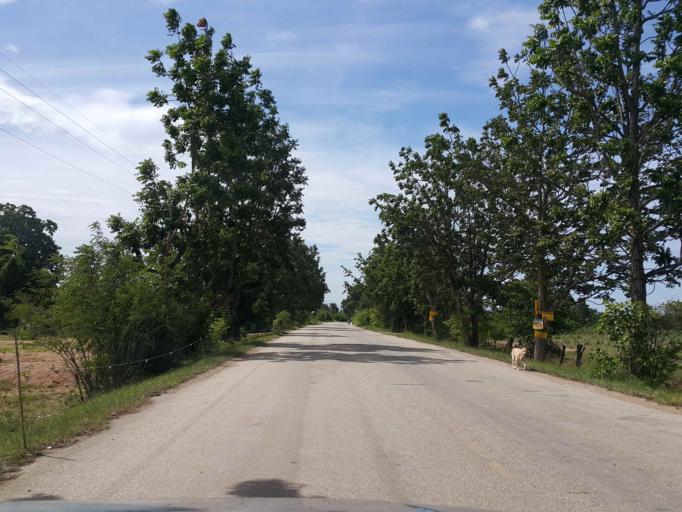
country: TH
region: Sukhothai
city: Ban Dan Lan Hoi
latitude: 17.1458
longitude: 99.5224
